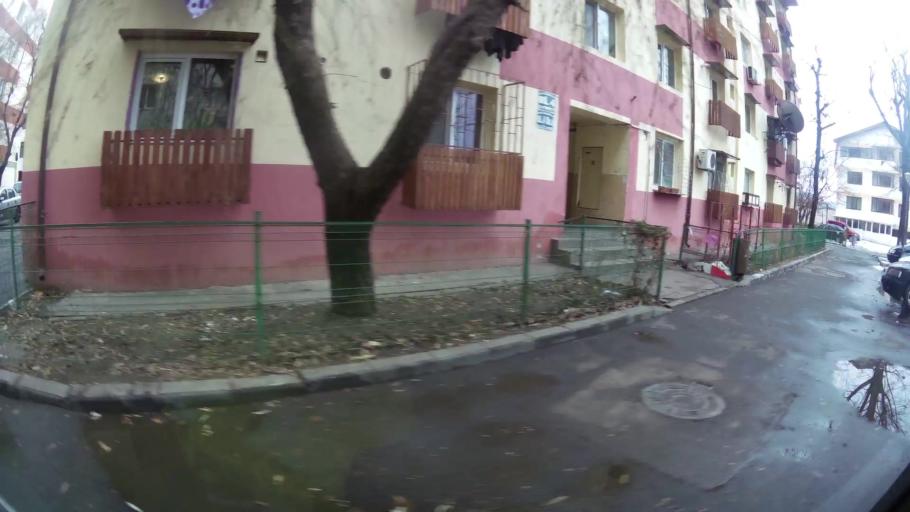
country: RO
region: Bucuresti
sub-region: Municipiul Bucuresti
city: Bucharest
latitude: 44.4151
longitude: 26.1265
